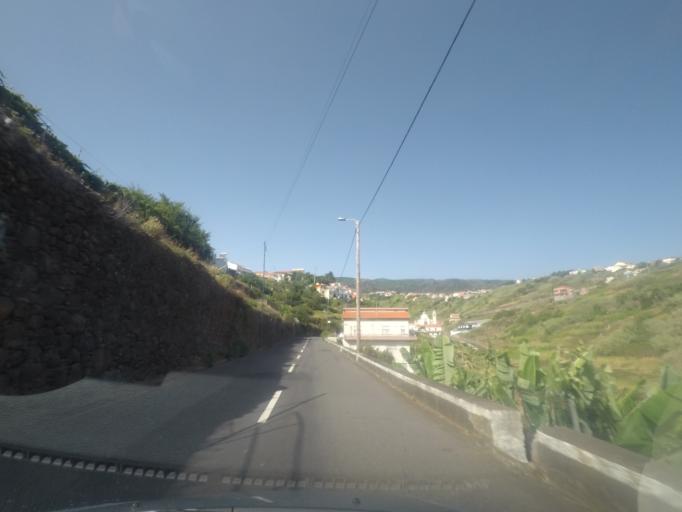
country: PT
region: Madeira
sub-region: Calheta
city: Arco da Calheta
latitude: 32.7274
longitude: -17.1643
